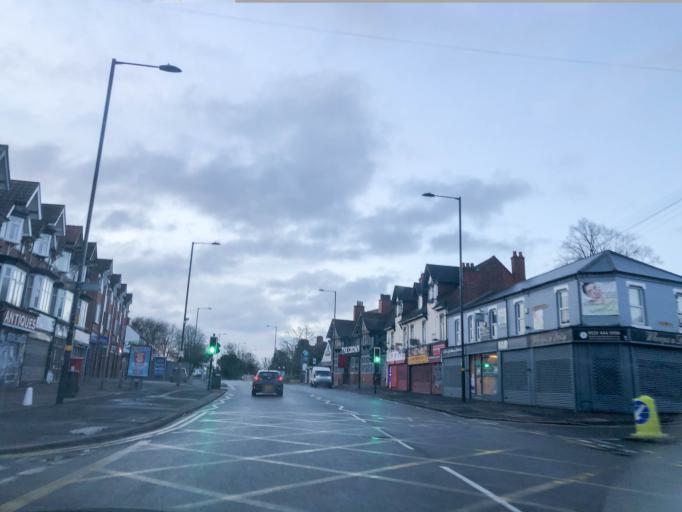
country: GB
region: England
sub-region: Solihull
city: Tidbury Green
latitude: 52.4220
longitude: -1.8922
